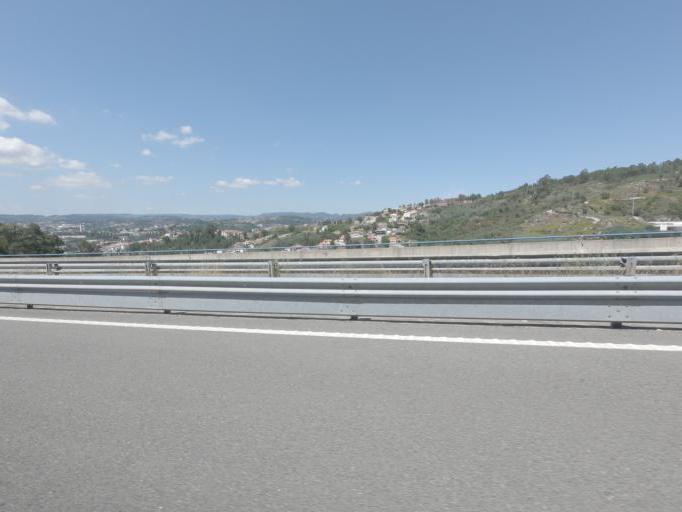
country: PT
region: Porto
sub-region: Amarante
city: Amarante
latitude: 41.2604
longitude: -8.0647
